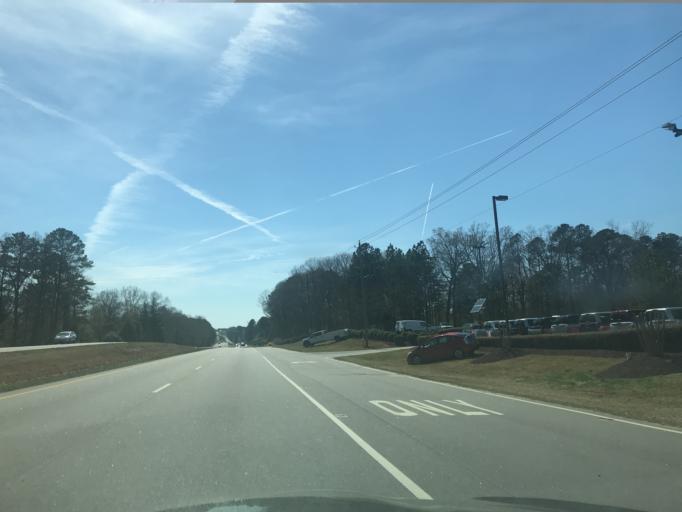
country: US
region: North Carolina
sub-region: Wake County
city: Fuquay-Varina
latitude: 35.6232
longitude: -78.7258
